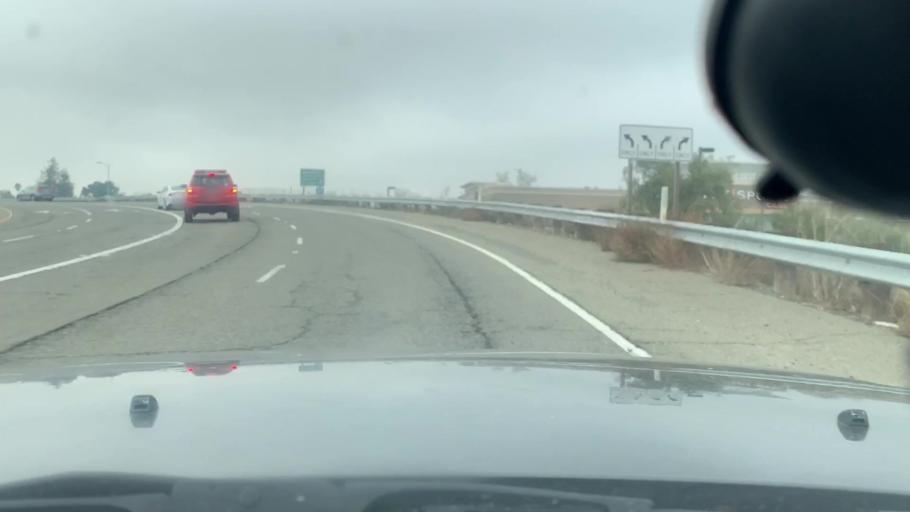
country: US
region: California
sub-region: Alameda County
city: Fremont
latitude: 37.5301
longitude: -122.0005
